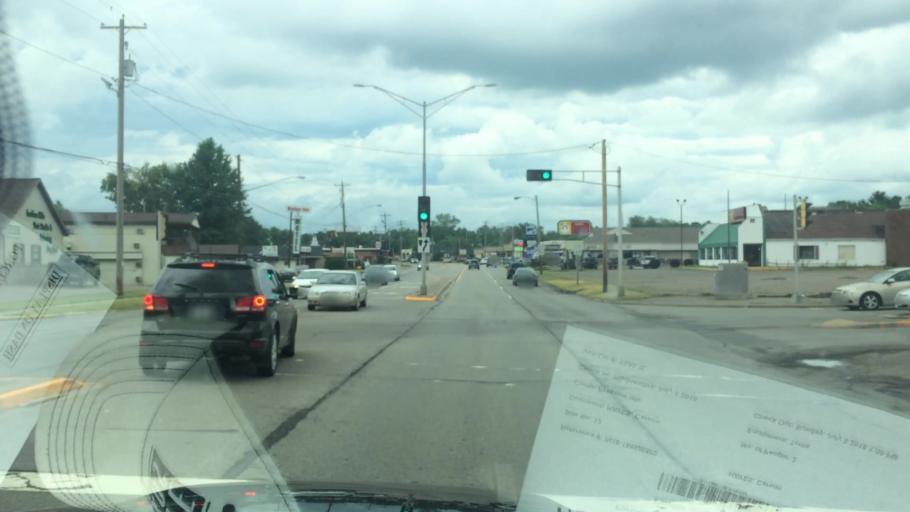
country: US
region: Wisconsin
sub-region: Marathon County
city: Schofield
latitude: 44.8989
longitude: -89.6112
